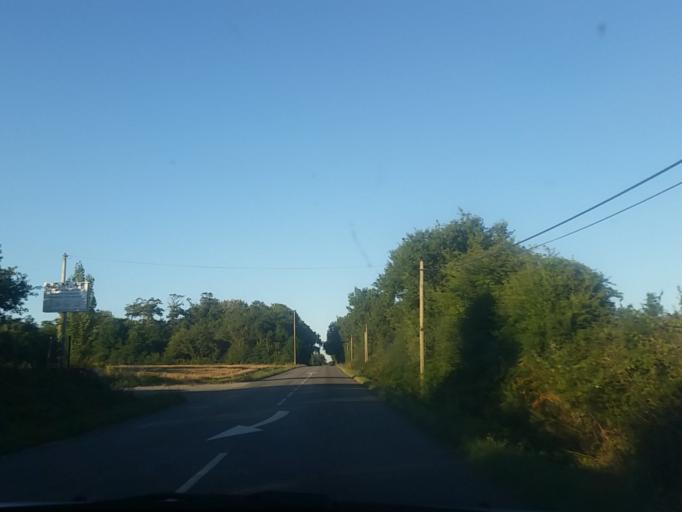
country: FR
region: Pays de la Loire
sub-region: Departement de la Loire-Atlantique
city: Saint-Michel-Chef-Chef
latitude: 47.1876
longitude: -2.1342
